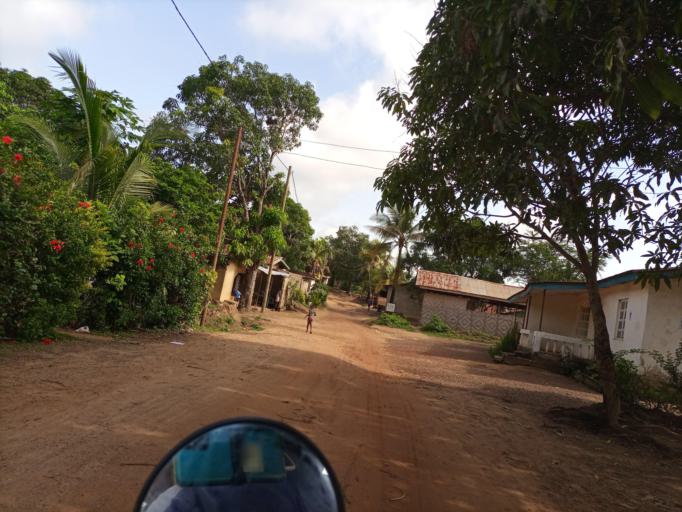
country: SL
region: Southern Province
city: Bo
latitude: 7.9646
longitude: -11.7610
